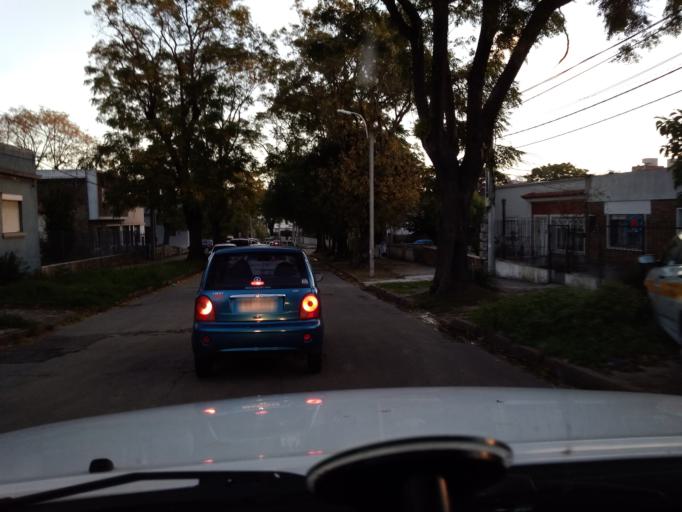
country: UY
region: Montevideo
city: Montevideo
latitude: -34.8603
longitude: -56.1743
